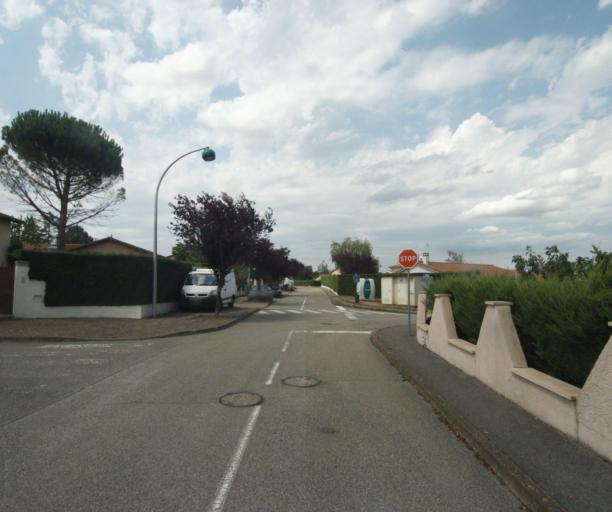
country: FR
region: Rhone-Alpes
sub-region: Departement du Rhone
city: Saint-Germain-Nuelles
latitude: 45.8434
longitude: 4.6071
